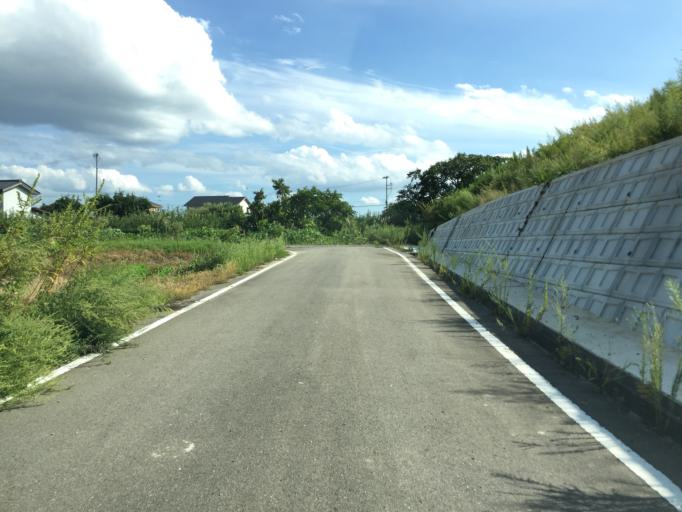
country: JP
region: Fukushima
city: Fukushima-shi
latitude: 37.7986
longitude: 140.4125
